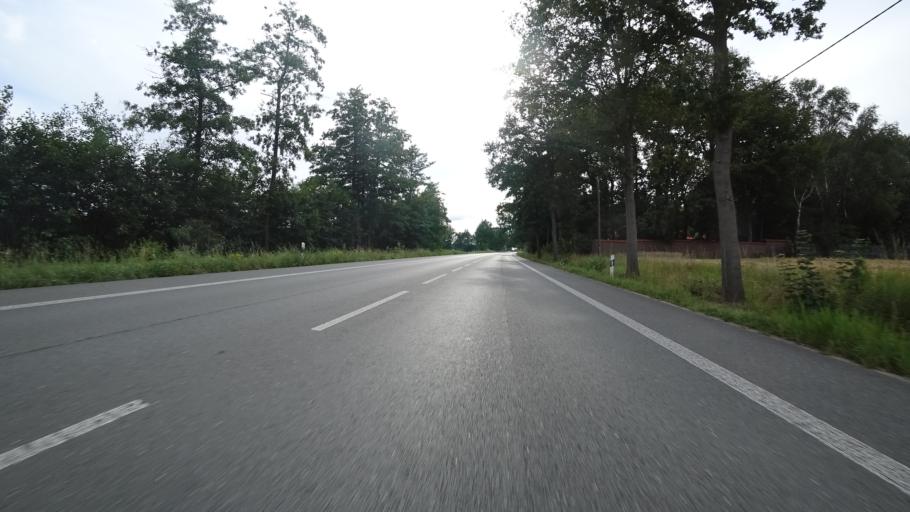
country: DE
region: North Rhine-Westphalia
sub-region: Regierungsbezirk Detmold
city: Guetersloh
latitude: 51.9212
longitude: 8.3437
